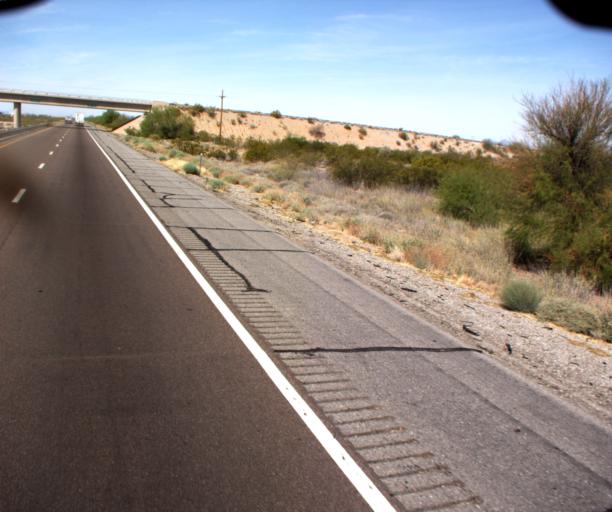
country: US
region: Arizona
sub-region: La Paz County
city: Salome
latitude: 33.5611
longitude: -113.2988
